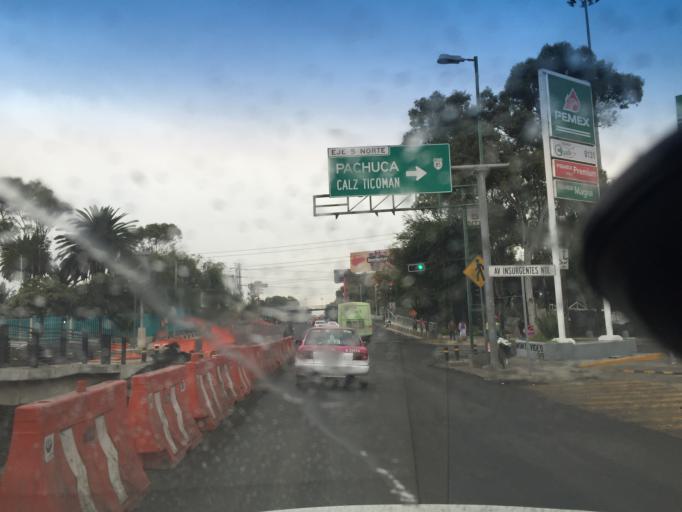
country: MX
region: Mexico
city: Colonia Lindavista
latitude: 19.4868
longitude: -99.1227
